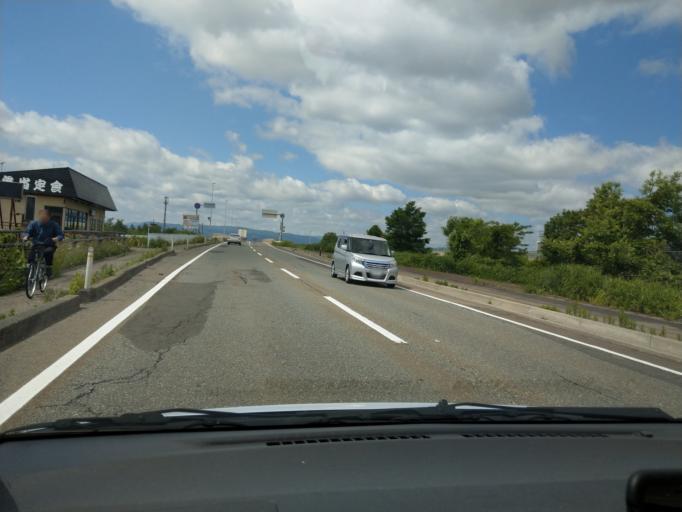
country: JP
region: Akita
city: Yuzawa
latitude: 39.2118
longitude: 140.5125
